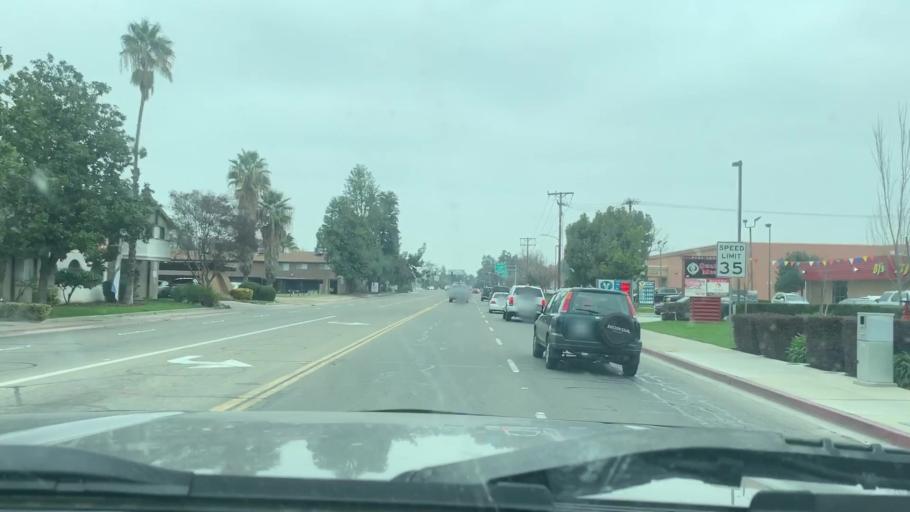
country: US
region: California
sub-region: Tulare County
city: Visalia
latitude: 36.3242
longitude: -119.3317
